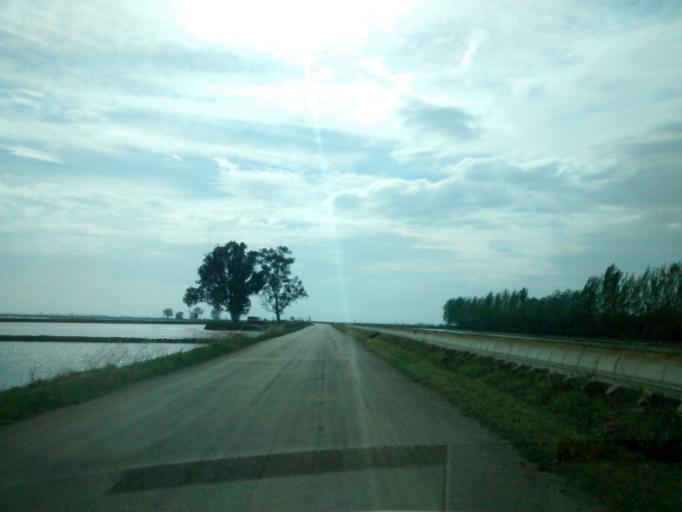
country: ES
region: Catalonia
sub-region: Provincia de Tarragona
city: Deltebre
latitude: 40.6929
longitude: 0.7945
